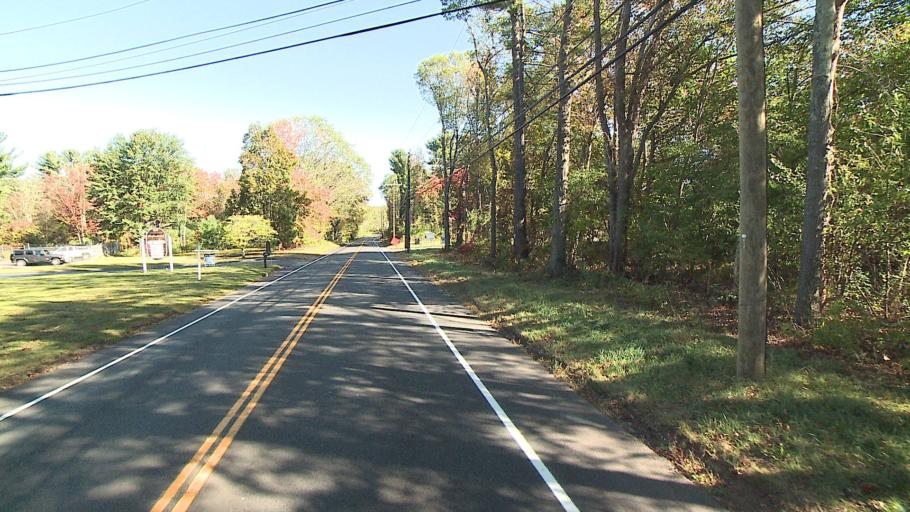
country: US
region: Connecticut
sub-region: Middlesex County
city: Lake Pocotopaug
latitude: 41.6017
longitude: -72.4869
